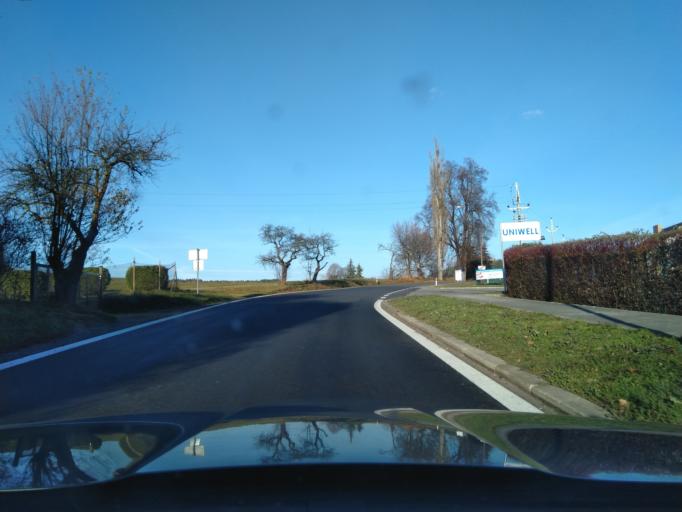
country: CZ
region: Jihocesky
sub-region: Okres Prachatice
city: Zdikov
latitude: 49.0868
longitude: 13.6941
